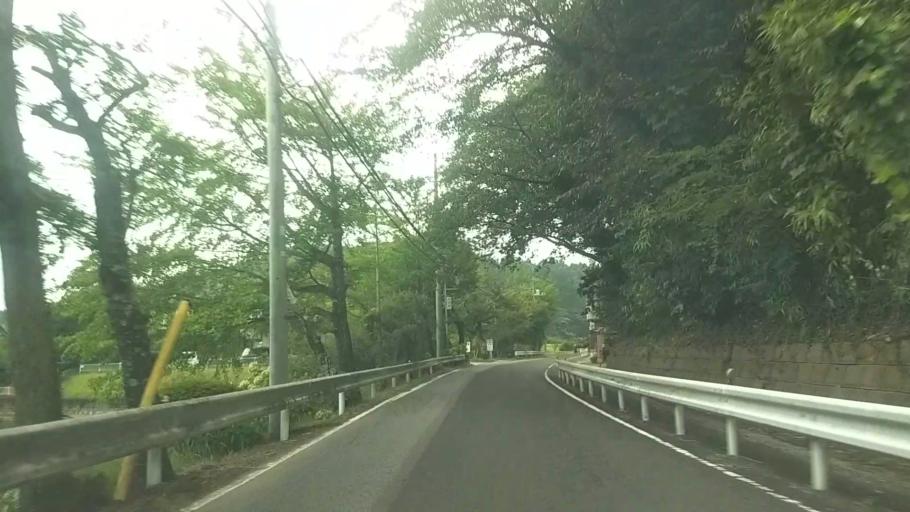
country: JP
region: Chiba
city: Kawaguchi
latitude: 35.2294
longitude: 140.0833
